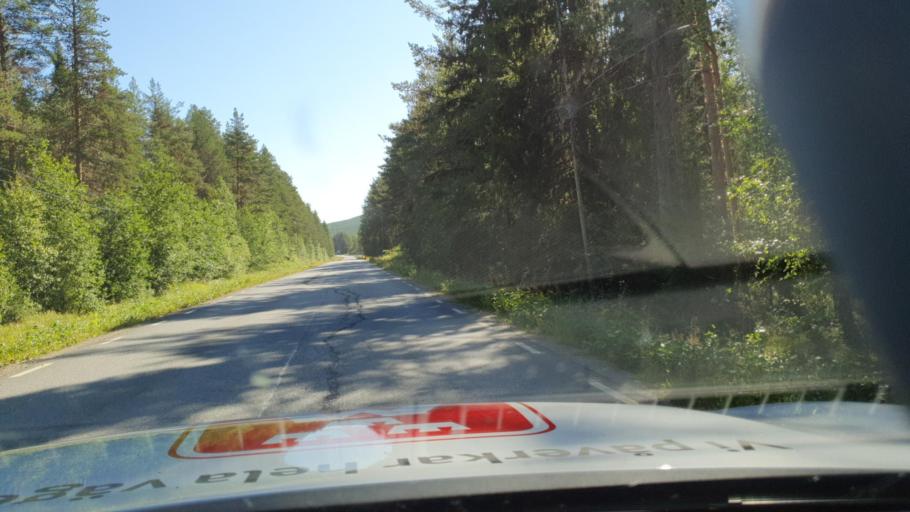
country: SE
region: Vaesterbotten
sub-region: Dorotea Kommun
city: Dorotea
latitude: 64.2628
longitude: 16.3659
